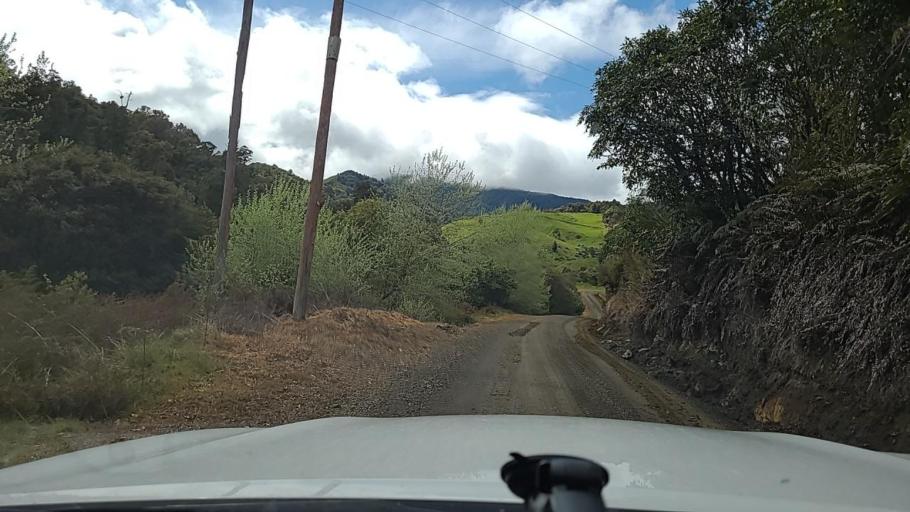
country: NZ
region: Bay of Plenty
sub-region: Opotiki District
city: Opotiki
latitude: -38.2508
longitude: 177.5985
